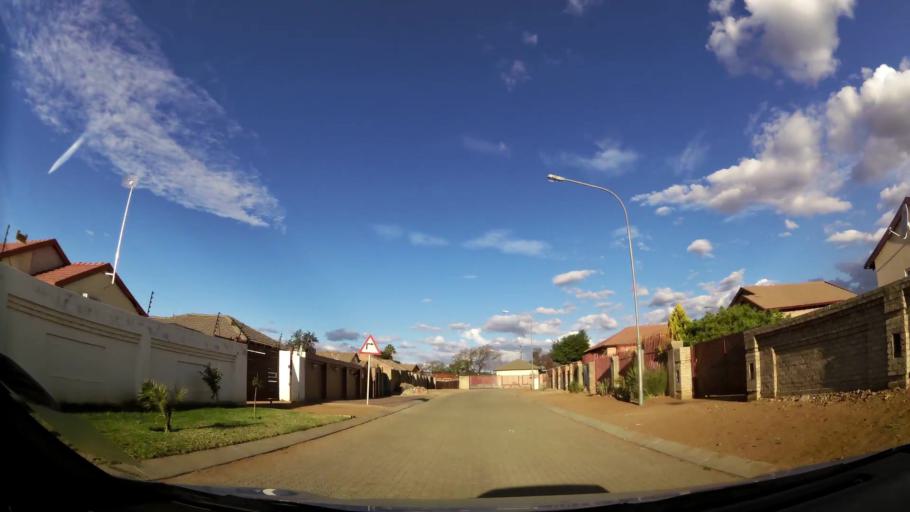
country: ZA
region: Limpopo
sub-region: Capricorn District Municipality
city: Polokwane
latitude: -23.9209
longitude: 29.4210
